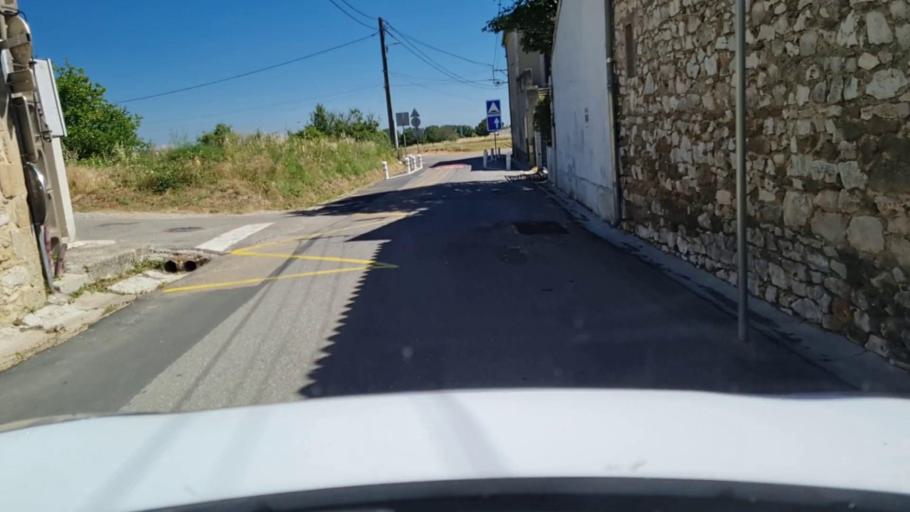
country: FR
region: Languedoc-Roussillon
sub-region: Departement du Gard
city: Saint-Mamert-du-Gard
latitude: 43.8543
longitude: 4.1586
